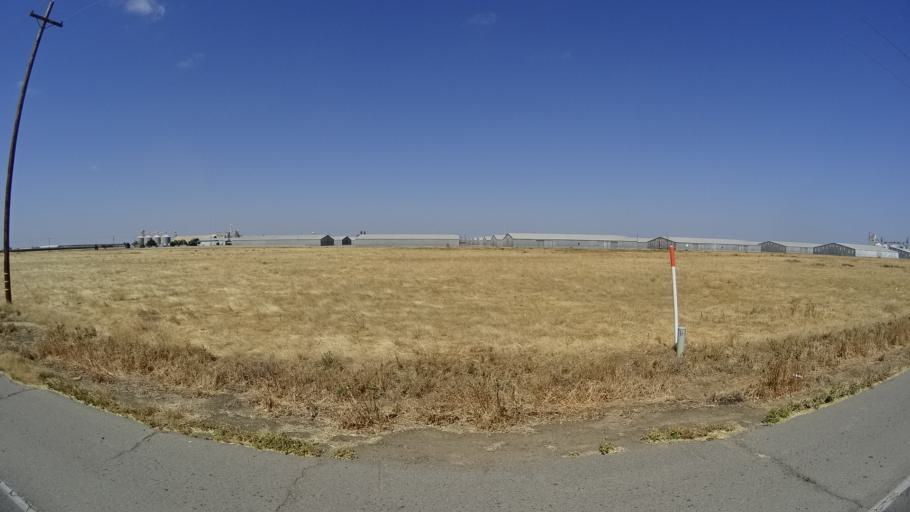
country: US
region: California
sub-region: Kings County
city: Home Garden
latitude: 36.2721
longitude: -119.6368
